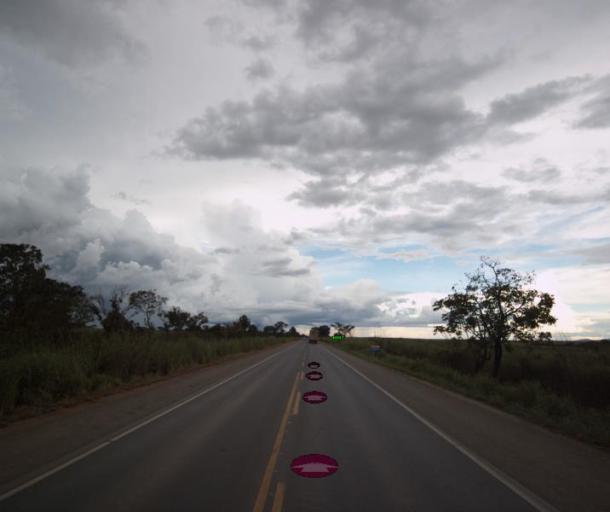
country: BR
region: Goias
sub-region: Itapaci
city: Itapaci
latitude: -14.9583
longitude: -49.3817
